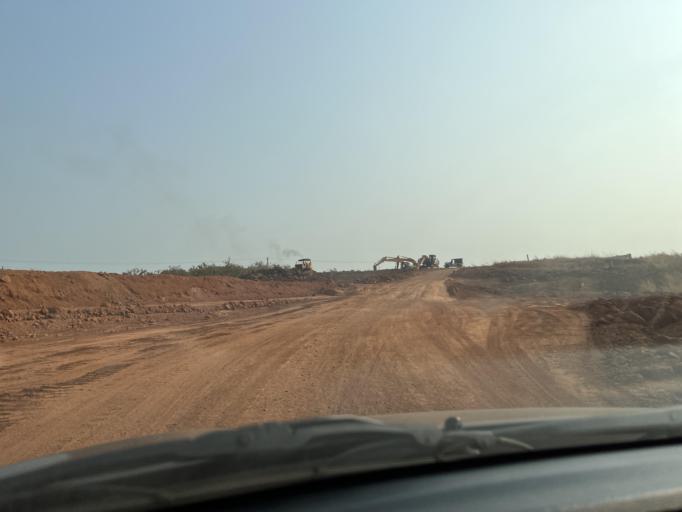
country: IN
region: Goa
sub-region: North Goa
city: Pernem
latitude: 15.6903
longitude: 73.8380
